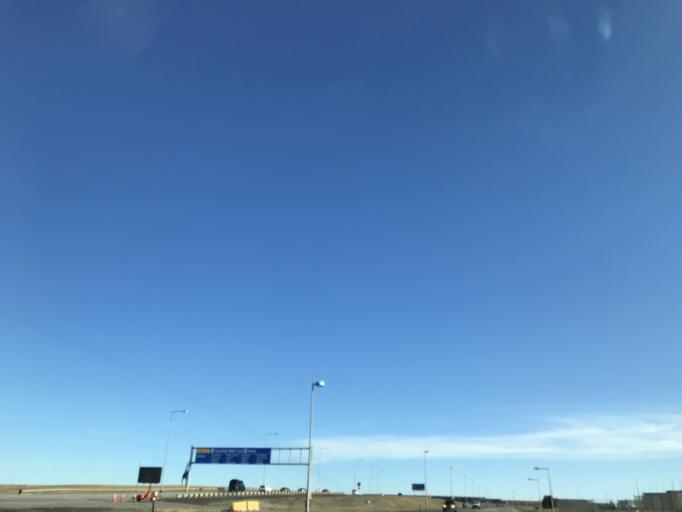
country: US
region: Colorado
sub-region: Weld County
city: Lochbuie
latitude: 39.8327
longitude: -104.6791
